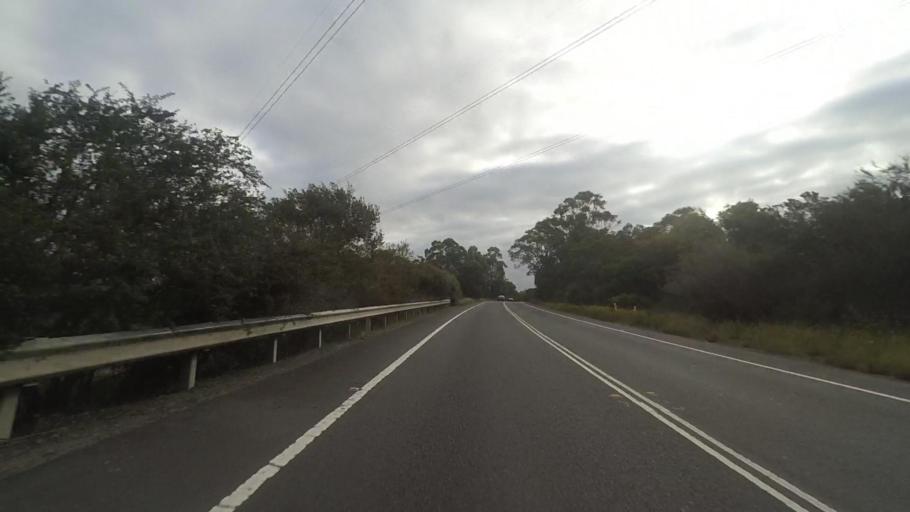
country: AU
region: New South Wales
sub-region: Sutherland Shire
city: Engadine
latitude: -34.0443
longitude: 150.9928
